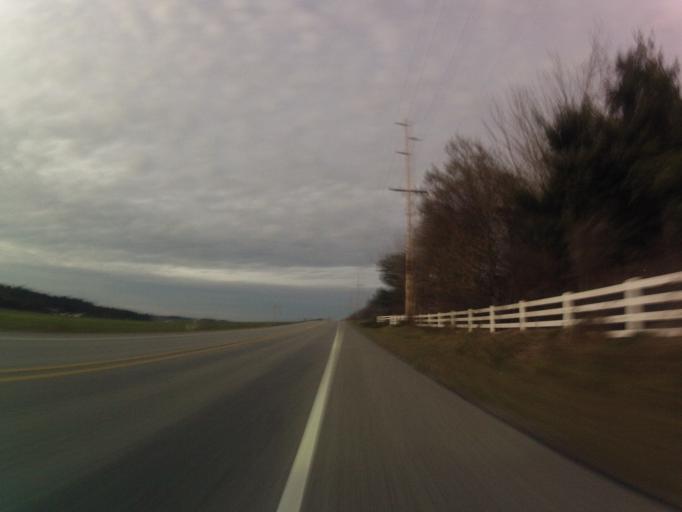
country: US
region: Washington
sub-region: Island County
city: Coupeville
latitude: 48.1806
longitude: -122.6880
